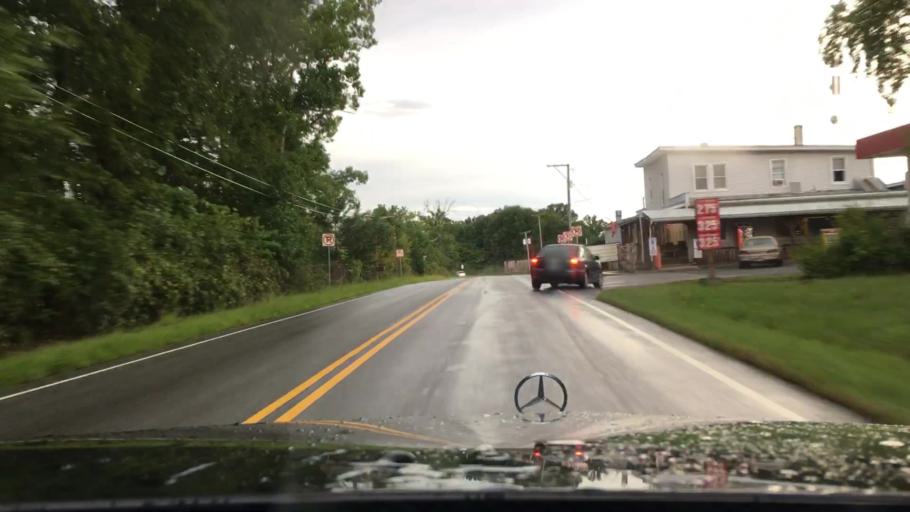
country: US
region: Virginia
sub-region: Amherst County
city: Amherst
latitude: 37.7150
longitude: -79.0218
